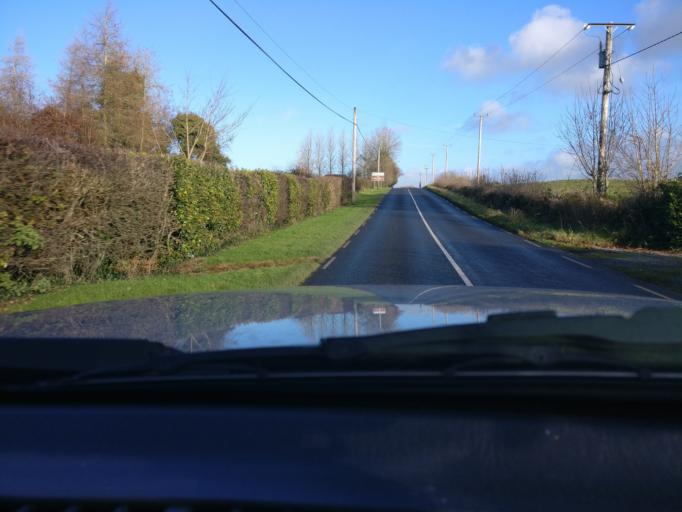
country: IE
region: Leinster
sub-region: An Iarmhi
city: Kilbeggan
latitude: 53.4738
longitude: -7.4543
